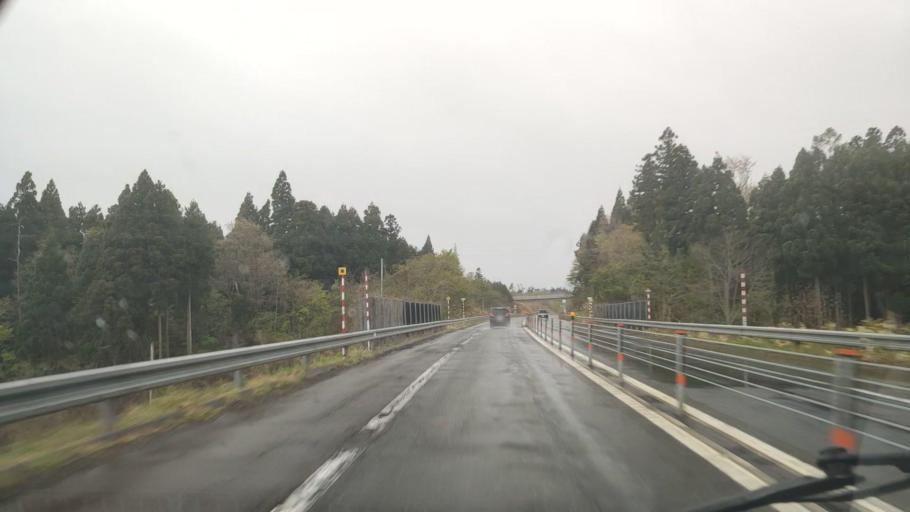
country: JP
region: Akita
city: Noshiromachi
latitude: 40.1667
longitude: 140.0494
